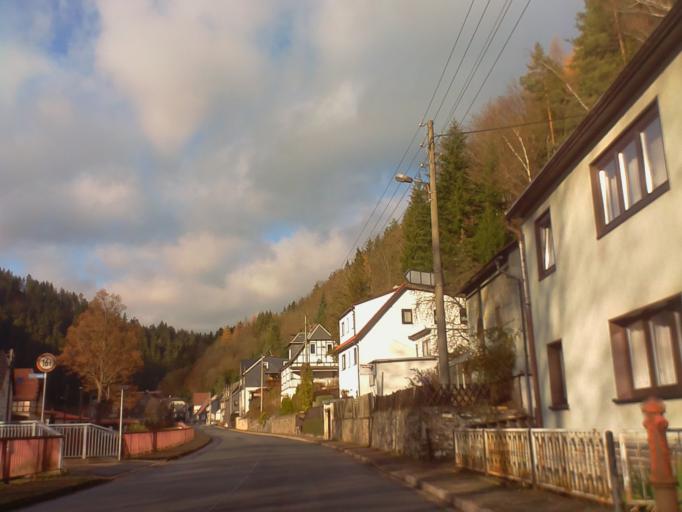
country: DE
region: Thuringia
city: Mellenbach-Glasbach
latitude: 50.5998
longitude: 11.1024
